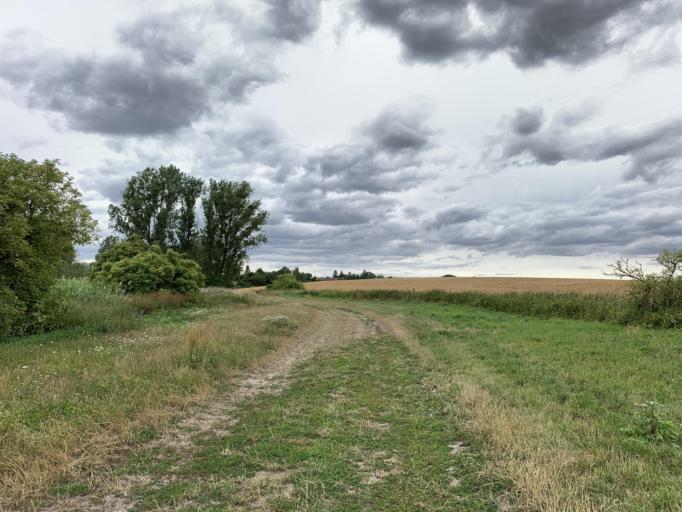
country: DE
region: Mecklenburg-Vorpommern
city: Blankensee
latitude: 53.3920
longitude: 13.2386
